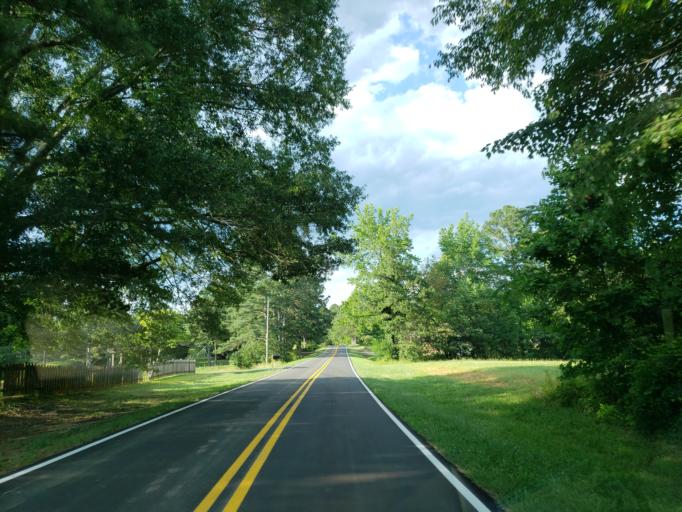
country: US
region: Georgia
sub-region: Haralson County
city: Buchanan
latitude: 33.8358
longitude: -85.2019
